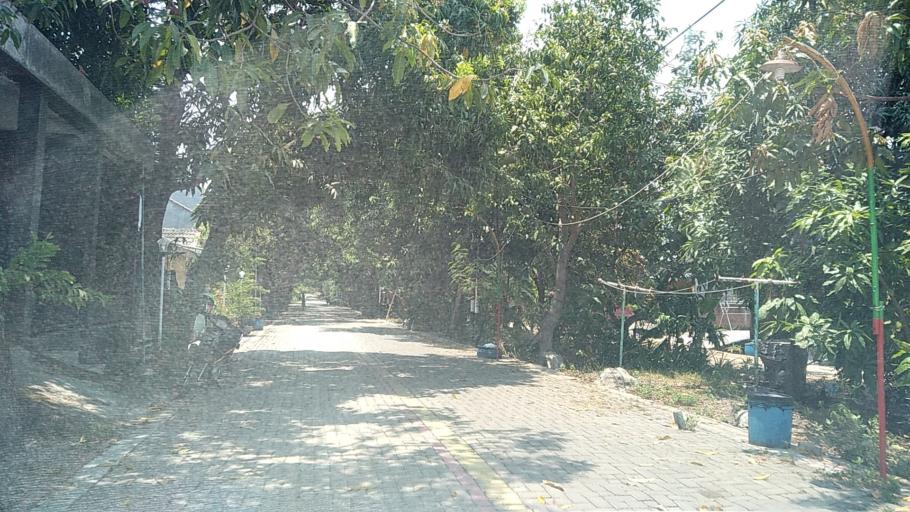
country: ID
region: Central Java
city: Semarang
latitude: -6.9782
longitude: 110.4769
